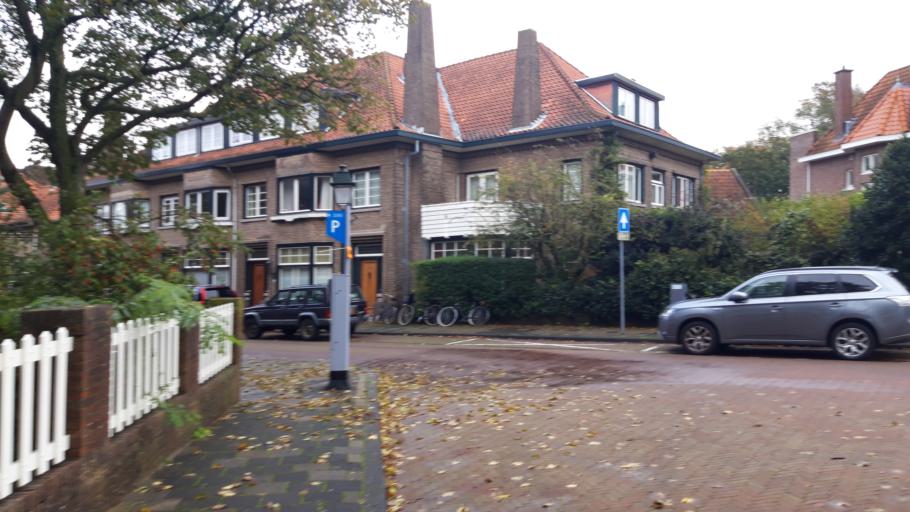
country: NL
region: South Holland
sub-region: Gemeente Den Haag
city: Scheveningen
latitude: 52.0999
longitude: 4.2785
